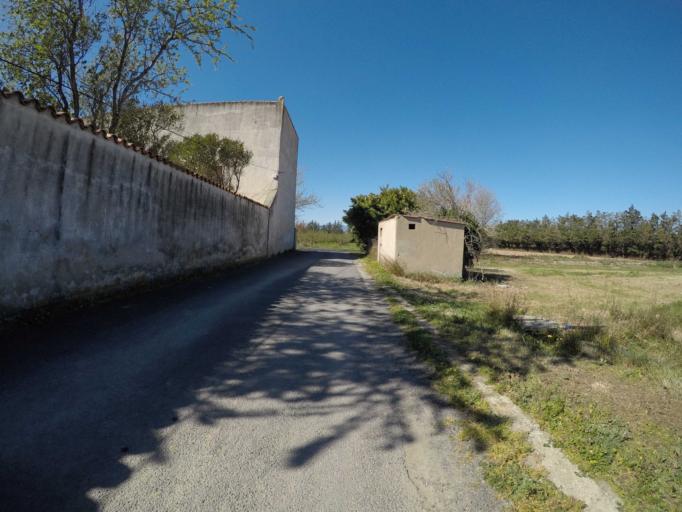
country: FR
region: Languedoc-Roussillon
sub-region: Departement des Pyrenees-Orientales
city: Ille-sur-Tet
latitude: 42.6851
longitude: 2.6552
